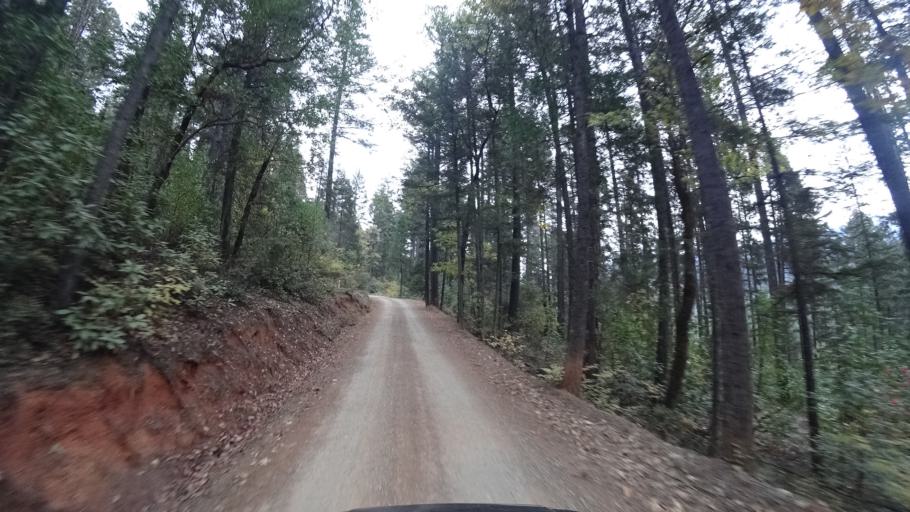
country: US
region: California
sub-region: Siskiyou County
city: Happy Camp
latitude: 41.7824
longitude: -123.3304
